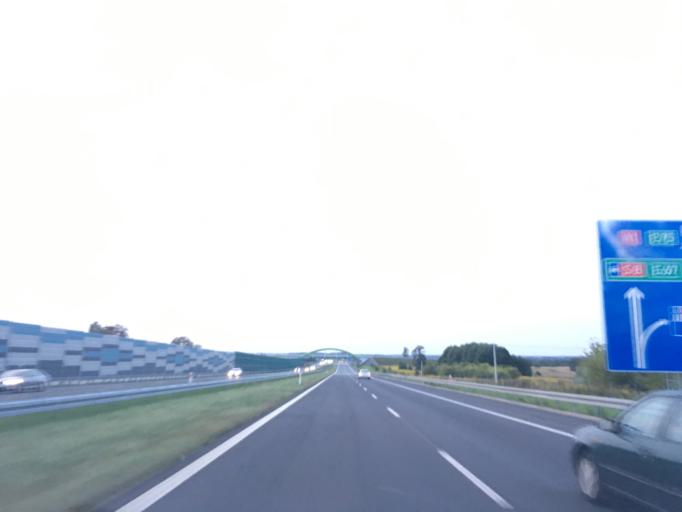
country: PL
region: Lodz Voivodeship
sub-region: Powiat zgierski
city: Strykow
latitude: 51.9169
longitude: 19.6208
